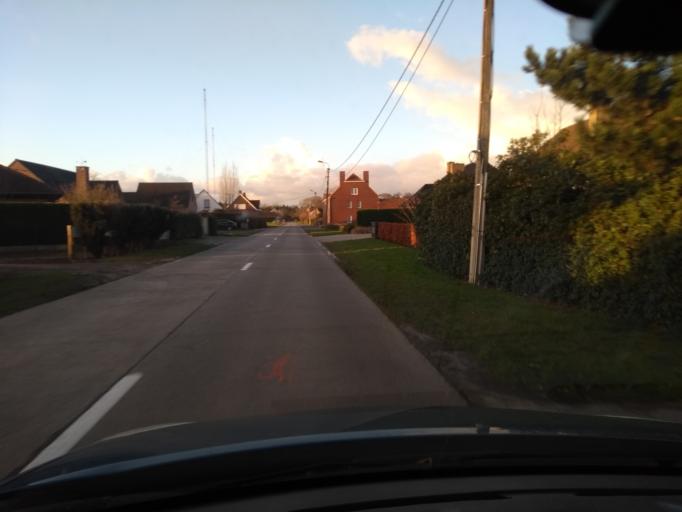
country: BE
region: Flanders
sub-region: Provincie West-Vlaanderen
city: Ruiselede
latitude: 51.0780
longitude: 3.3522
